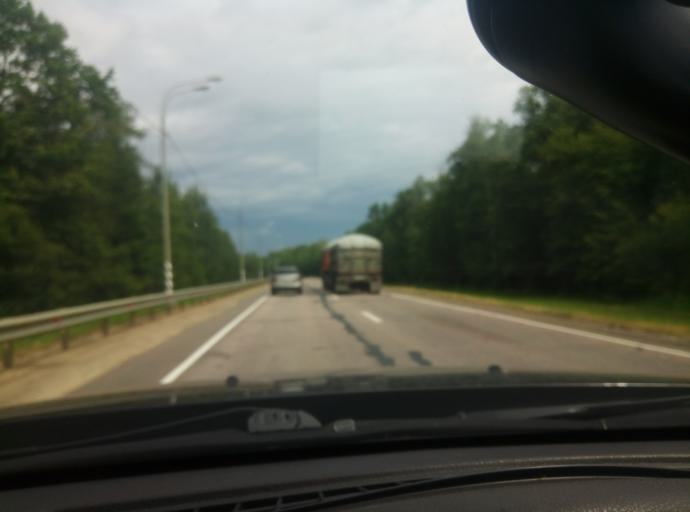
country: RU
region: Tula
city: Leninskiy
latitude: 54.4077
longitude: 37.5019
